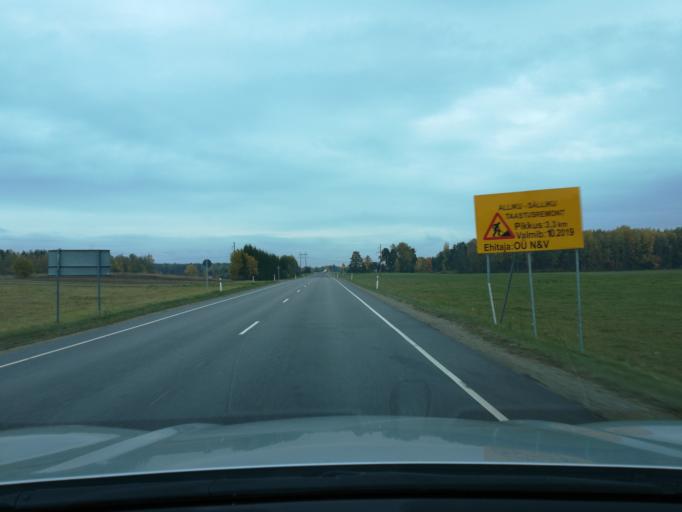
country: EE
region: Ida-Virumaa
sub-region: Johvi vald
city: Johvi
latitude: 59.0809
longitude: 27.3159
